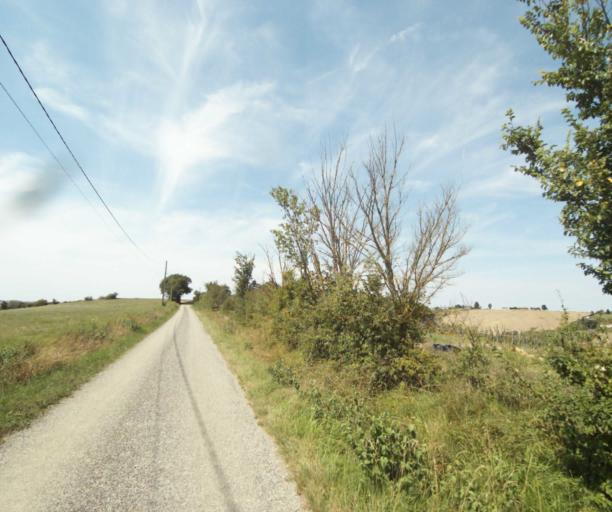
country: FR
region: Midi-Pyrenees
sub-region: Departement de la Haute-Garonne
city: Gaillac-Toulza
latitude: 43.2271
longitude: 1.4091
